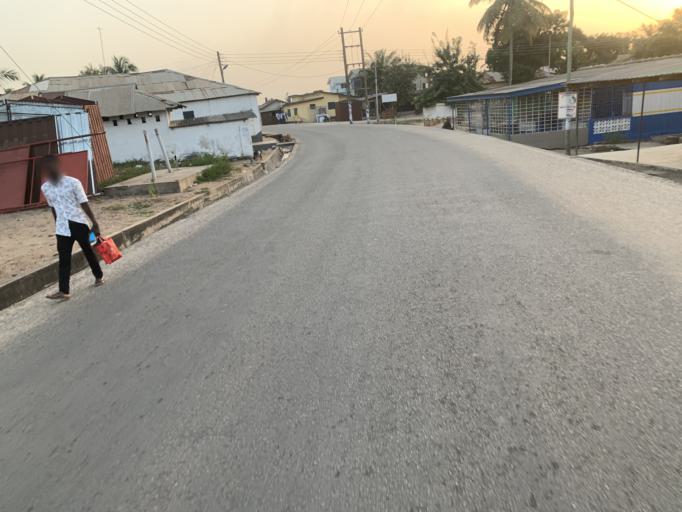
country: GH
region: Central
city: Winneba
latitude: 5.3502
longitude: -0.6240
